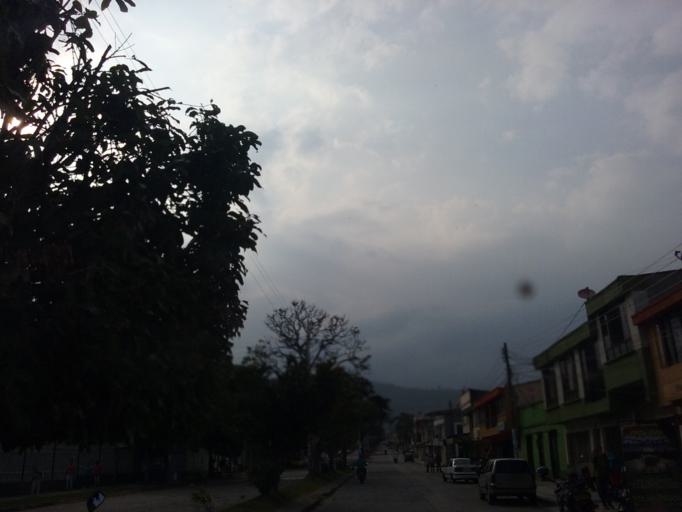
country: CO
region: Tolima
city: Libano
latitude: 4.9219
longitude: -75.0576
